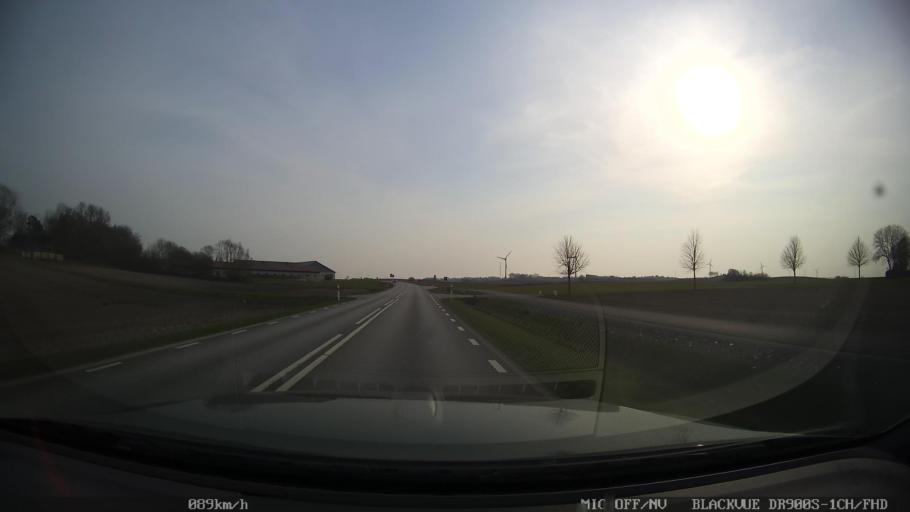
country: SE
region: Skane
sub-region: Ystads Kommun
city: Ystad
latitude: 55.4730
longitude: 13.7981
